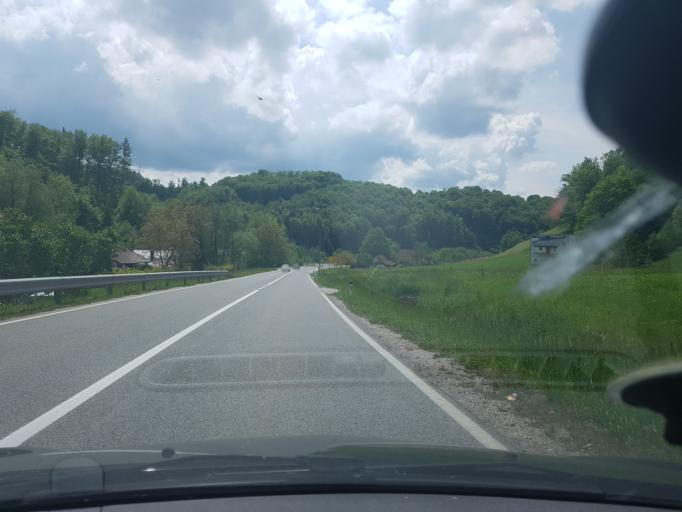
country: SI
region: Rogaska Slatina
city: Rogaska Slatina
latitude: 46.2422
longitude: 15.6054
